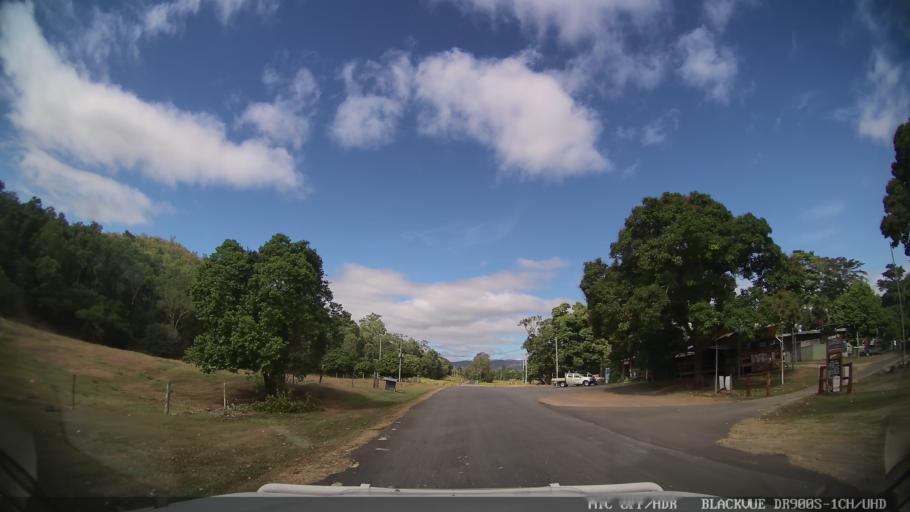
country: AU
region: Queensland
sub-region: Cook
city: Cooktown
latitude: -15.7056
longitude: 145.2238
